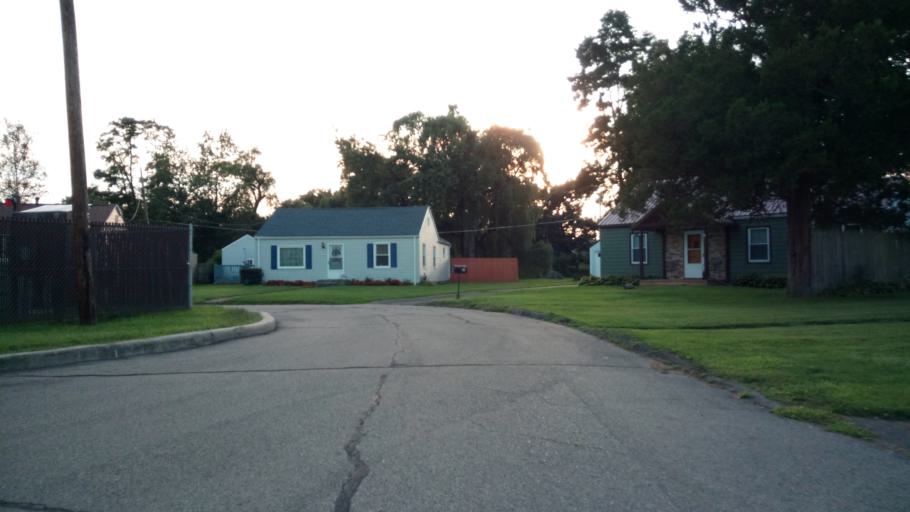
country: US
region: New York
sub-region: Chemung County
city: Elmira
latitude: 42.0722
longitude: -76.7906
